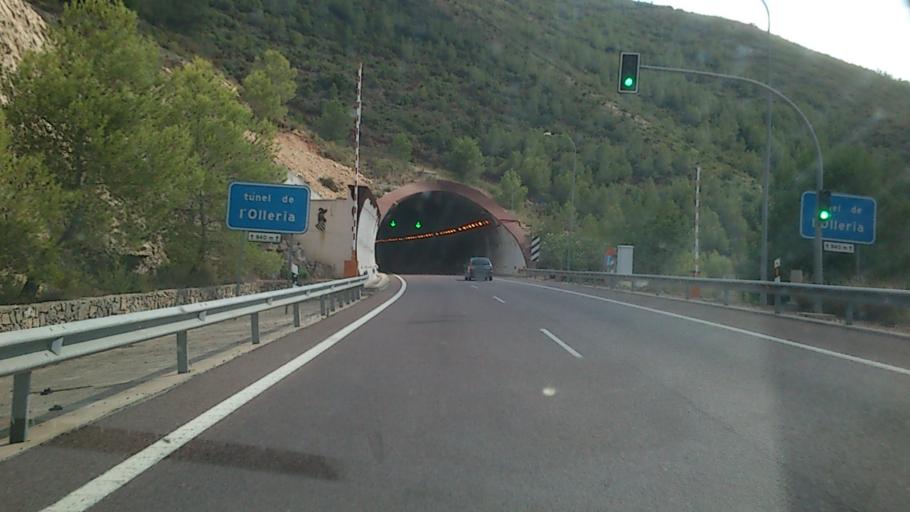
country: ES
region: Valencia
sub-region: Provincia de Valencia
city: L'Olleria
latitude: 38.9278
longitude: -0.5755
